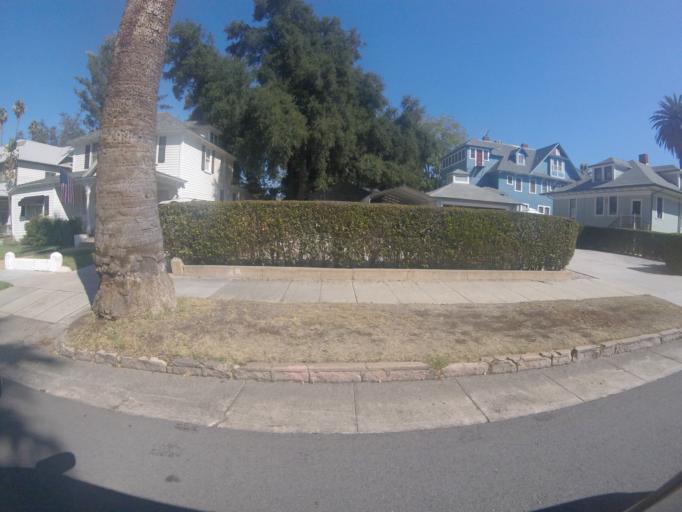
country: US
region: California
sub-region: San Bernardino County
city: Redlands
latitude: 34.0524
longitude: -117.1846
